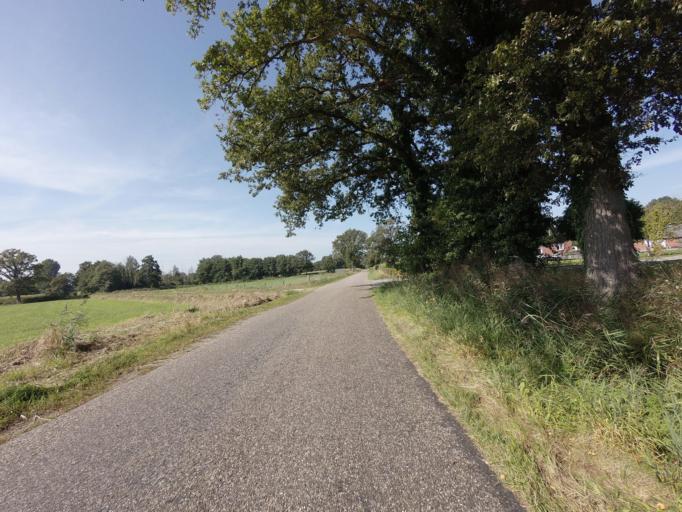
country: NL
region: Overijssel
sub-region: Gemeente Haaksbergen
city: Haaksbergen
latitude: 52.2062
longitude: 6.7711
